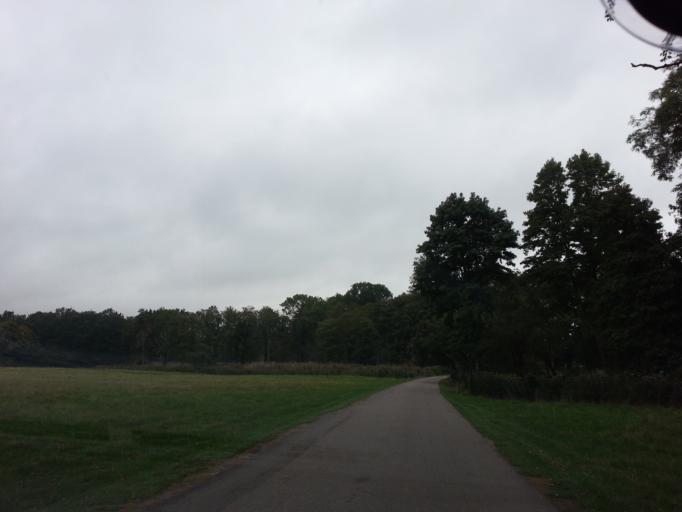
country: DK
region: Zealand
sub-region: Lolland Kommune
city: Maribo
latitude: 54.8279
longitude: 11.4936
